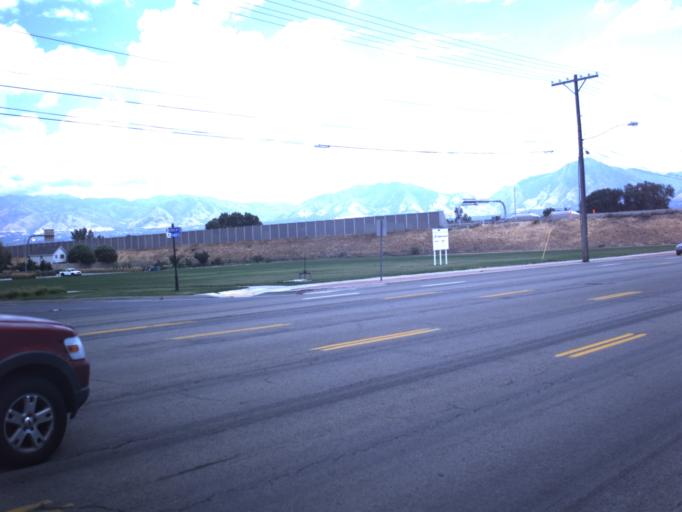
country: US
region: Utah
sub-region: Salt Lake County
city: Taylorsville
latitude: 40.6530
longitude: -111.9557
